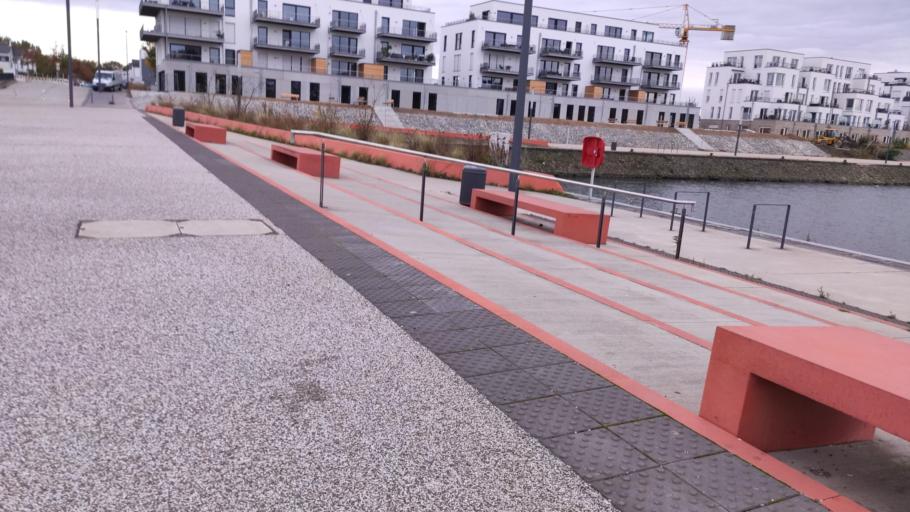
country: DE
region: North Rhine-Westphalia
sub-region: Regierungsbezirk Munster
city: Gelsenkirchen
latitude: 51.5455
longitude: 7.0984
